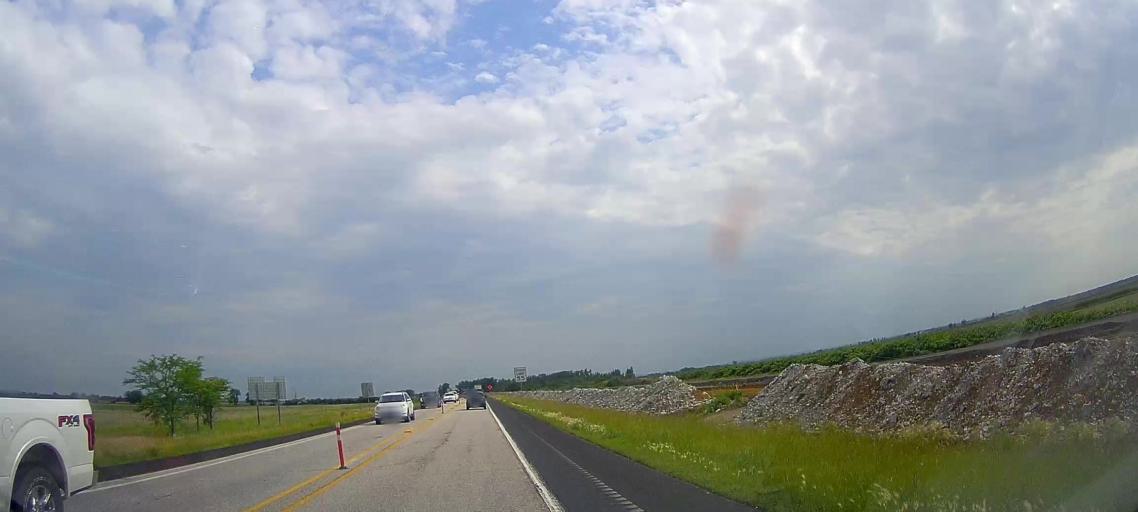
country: US
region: Nebraska
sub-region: Washington County
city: Blair
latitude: 41.6896
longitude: -96.0418
